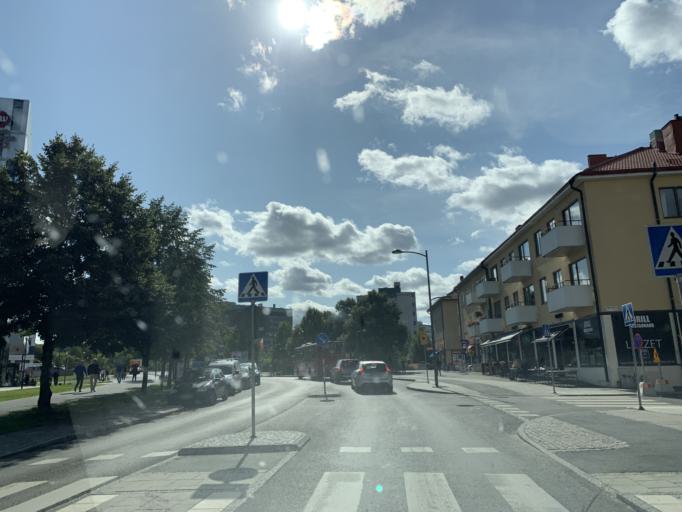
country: SE
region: Stockholm
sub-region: Sundbybergs Kommun
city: Sundbyberg
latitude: 59.3575
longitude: 17.9751
